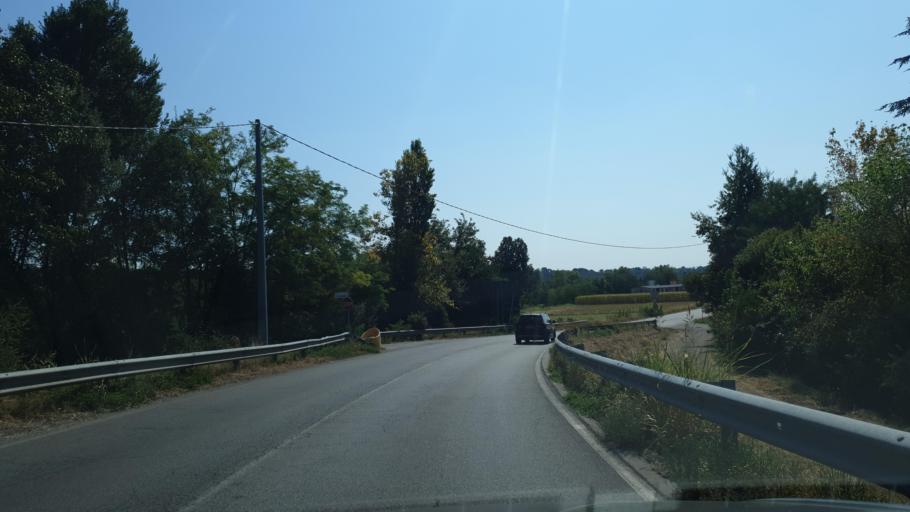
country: IT
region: Lombardy
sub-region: Provincia di Brescia
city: Prevalle
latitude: 45.5506
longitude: 10.4338
